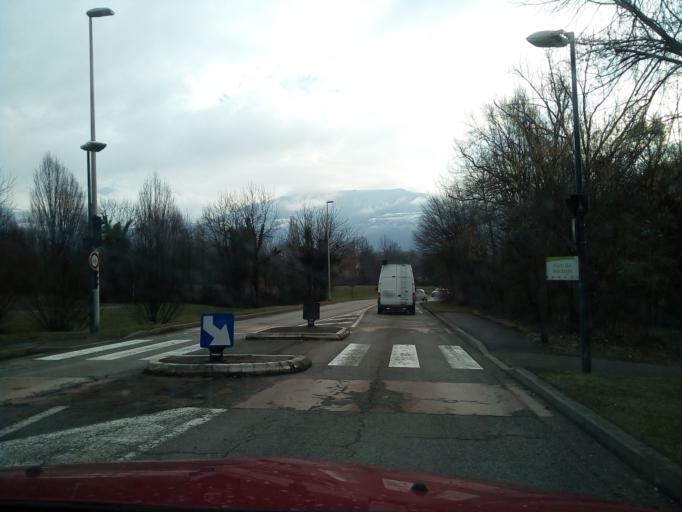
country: FR
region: Rhone-Alpes
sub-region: Departement de l'Isere
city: Corenc
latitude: 45.2132
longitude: 5.7805
